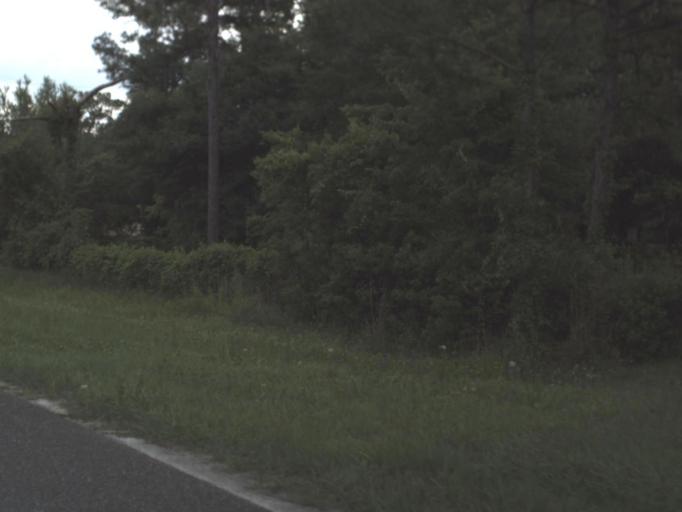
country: US
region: Florida
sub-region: Columbia County
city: Five Points
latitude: 30.2453
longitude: -82.6384
